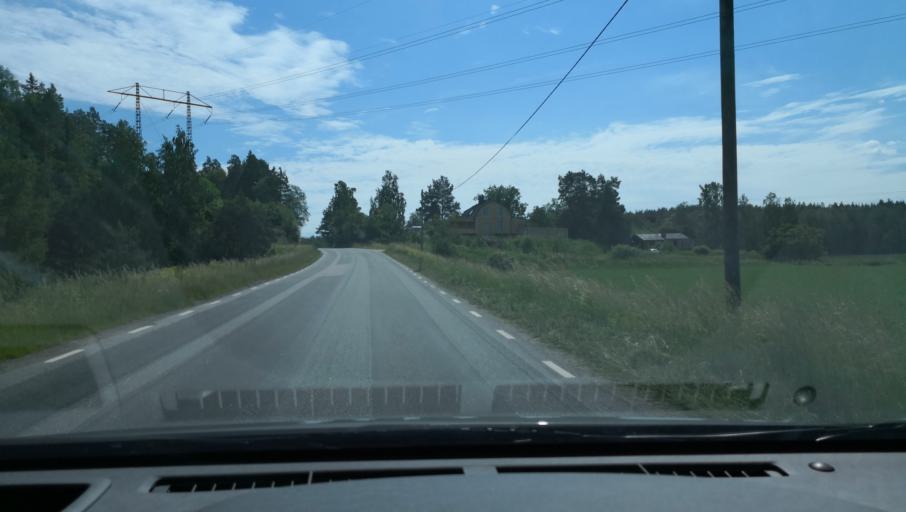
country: SE
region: Uppsala
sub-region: Habo Kommun
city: Balsta
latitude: 59.6612
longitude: 17.4502
